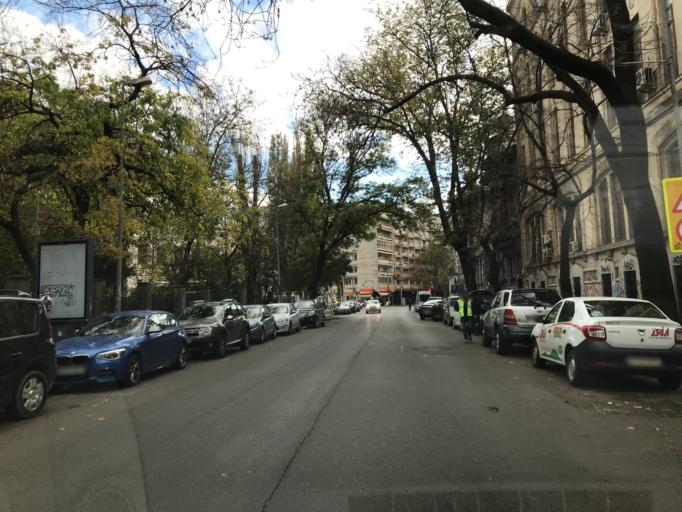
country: RO
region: Bucuresti
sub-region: Municipiul Bucuresti
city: Bucuresti
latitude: 44.4355
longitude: 26.0893
